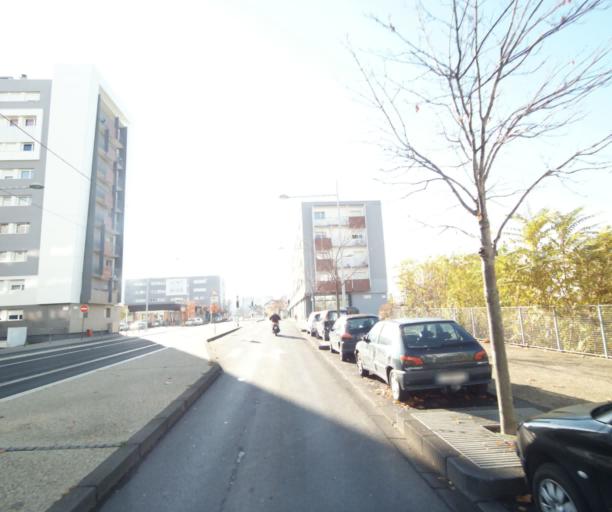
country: FR
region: Auvergne
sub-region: Departement du Puy-de-Dome
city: Beaumont
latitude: 45.7642
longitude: 3.0890
